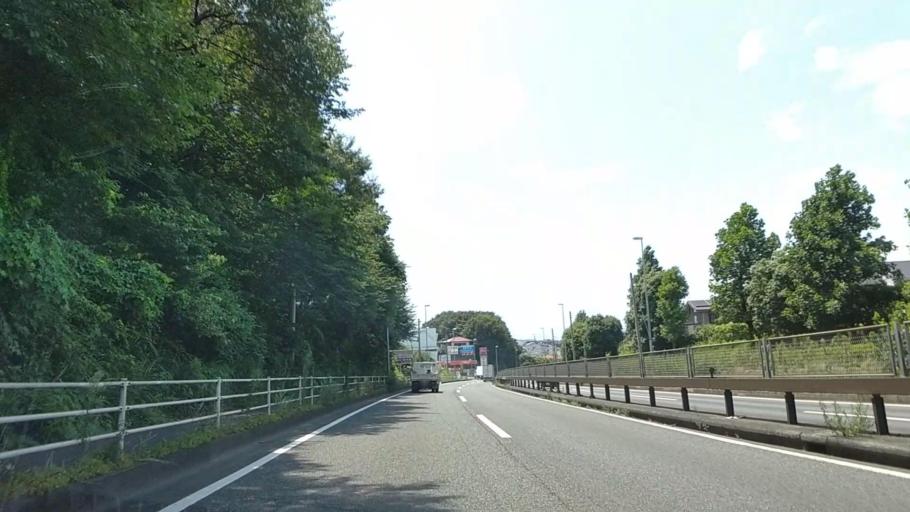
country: JP
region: Kanagawa
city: Zama
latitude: 35.4658
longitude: 139.4058
